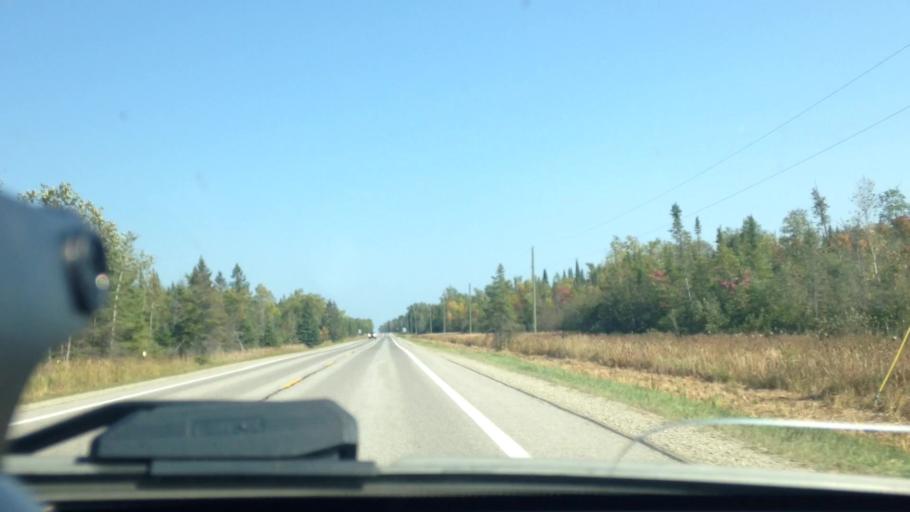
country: US
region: Michigan
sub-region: Luce County
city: Newberry
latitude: 46.3035
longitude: -85.3844
